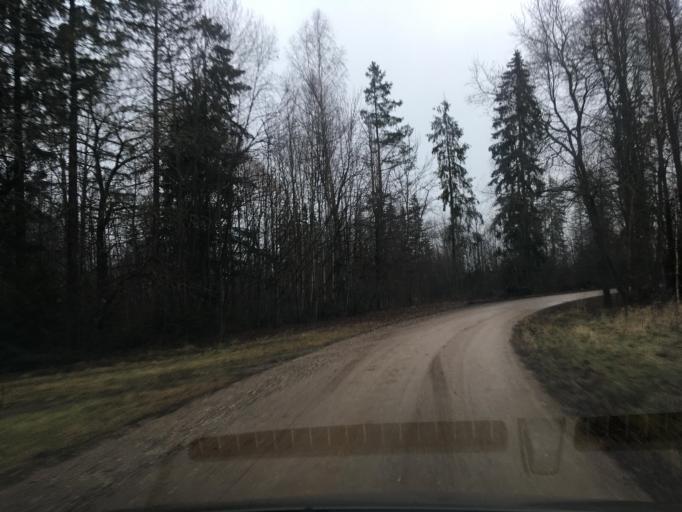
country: EE
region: Tartu
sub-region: Tartu linn
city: Tartu
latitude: 58.3782
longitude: 26.9263
